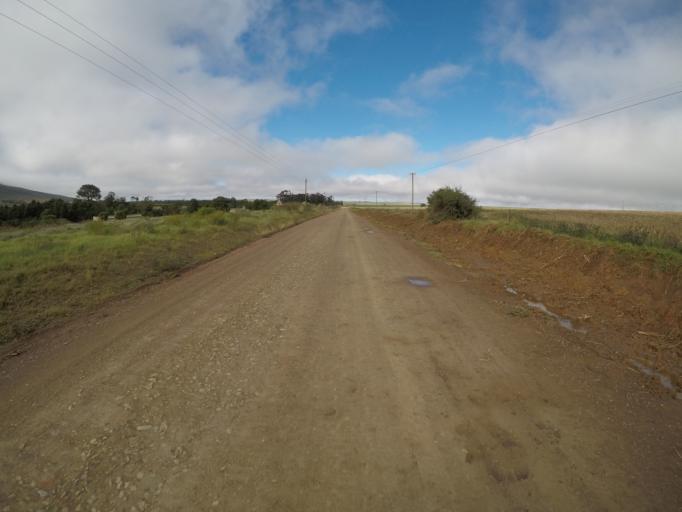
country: ZA
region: Western Cape
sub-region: Cape Winelands District Municipality
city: Ashton
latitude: -34.1343
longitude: 19.8570
